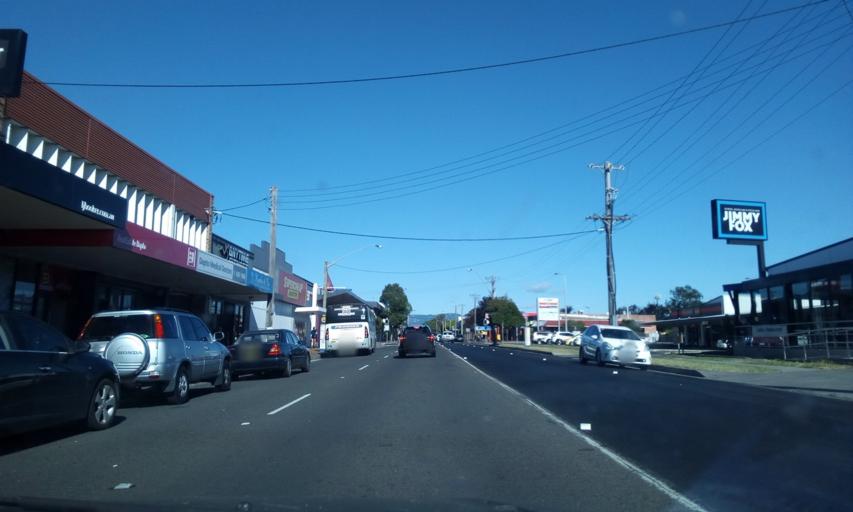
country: AU
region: New South Wales
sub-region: Wollongong
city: Dapto
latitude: -34.4920
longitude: 150.7959
